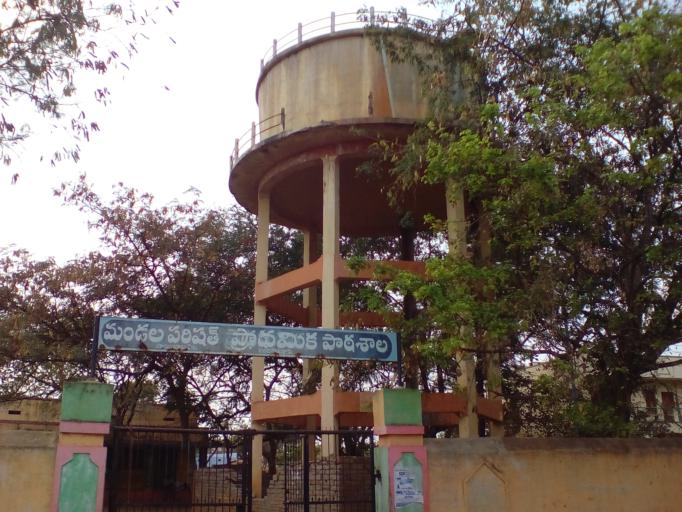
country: IN
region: Andhra Pradesh
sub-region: Kurnool
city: Nandikotkur
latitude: 15.8502
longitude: 78.2633
